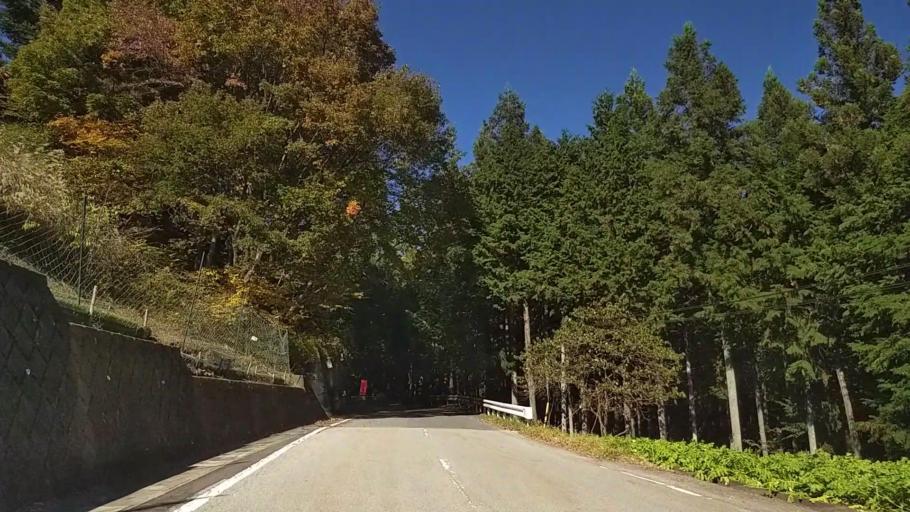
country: JP
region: Yamanashi
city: Otsuki
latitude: 35.7455
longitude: 138.9647
